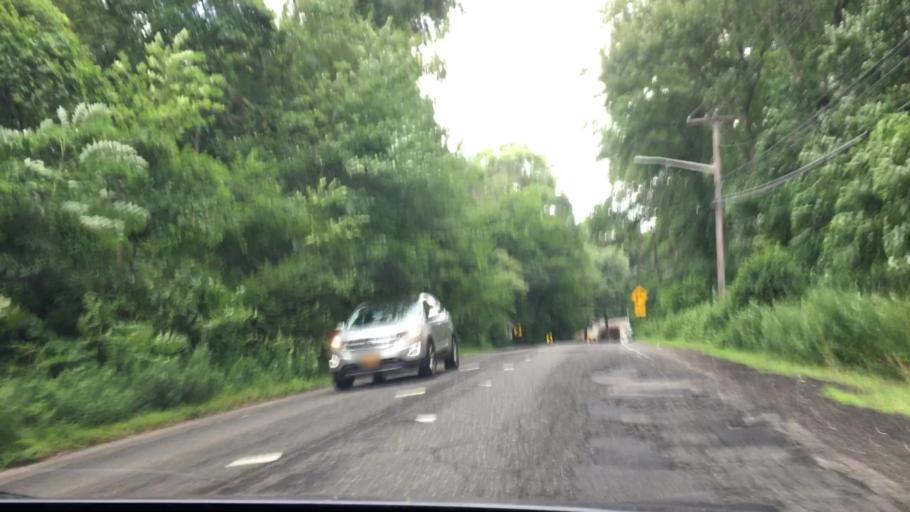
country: US
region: New York
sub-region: Suffolk County
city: West Hills
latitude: 40.8112
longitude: -73.4431
